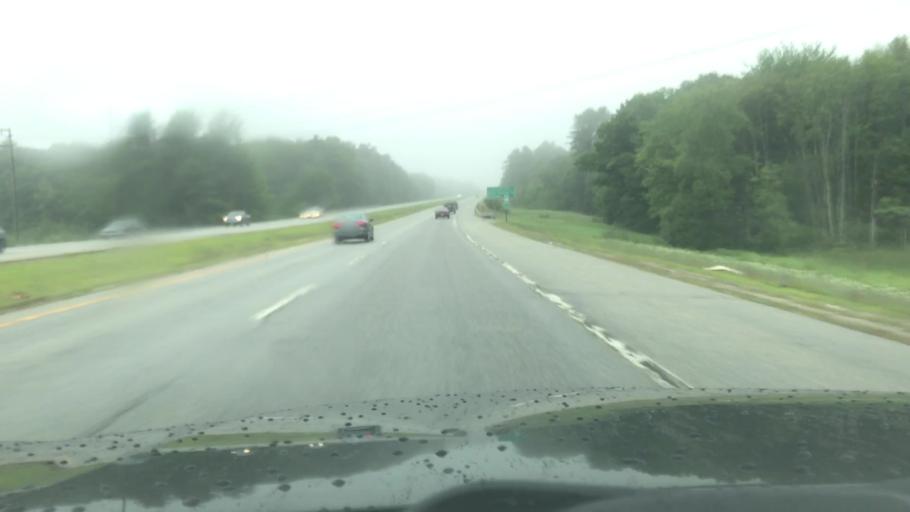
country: US
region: Maine
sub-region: Cumberland County
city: South Portland Gardens
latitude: 43.6098
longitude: -70.3200
